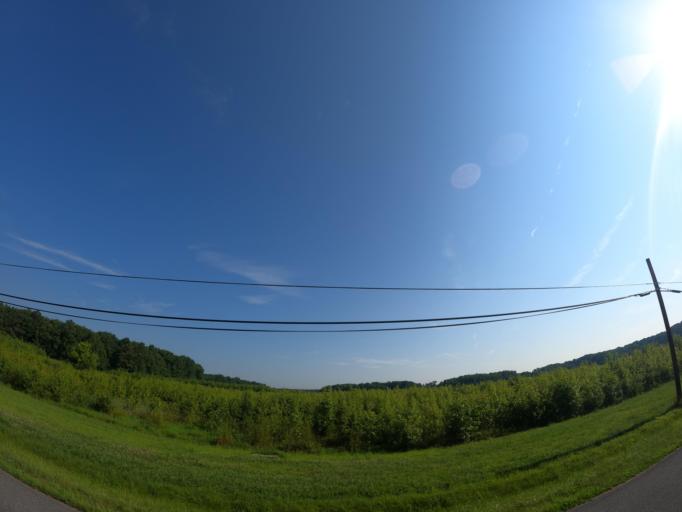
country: US
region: Delaware
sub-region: Sussex County
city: Georgetown
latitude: 38.6980
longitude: -75.4339
